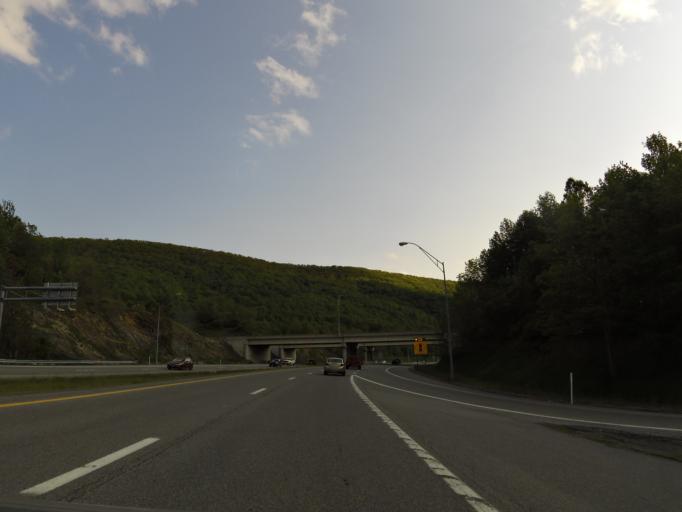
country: US
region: West Virginia
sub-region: Mercer County
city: Bluefield
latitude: 37.2755
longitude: -81.1638
